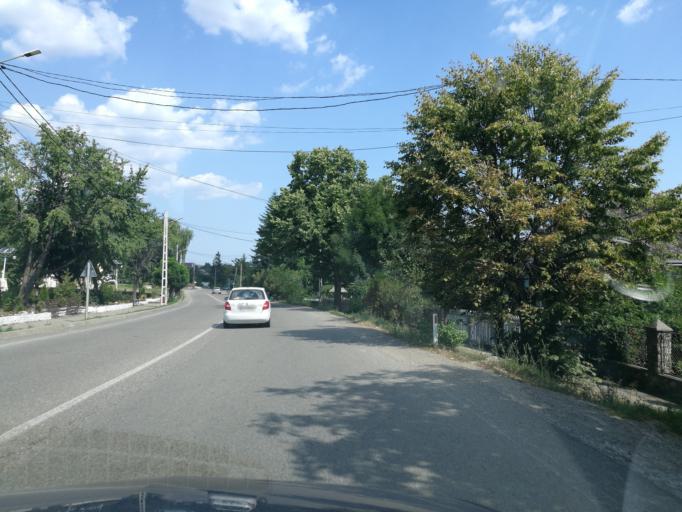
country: RO
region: Neamt
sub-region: Comuna Baltatesti
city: Baltatesti
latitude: 47.1218
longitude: 26.3100
